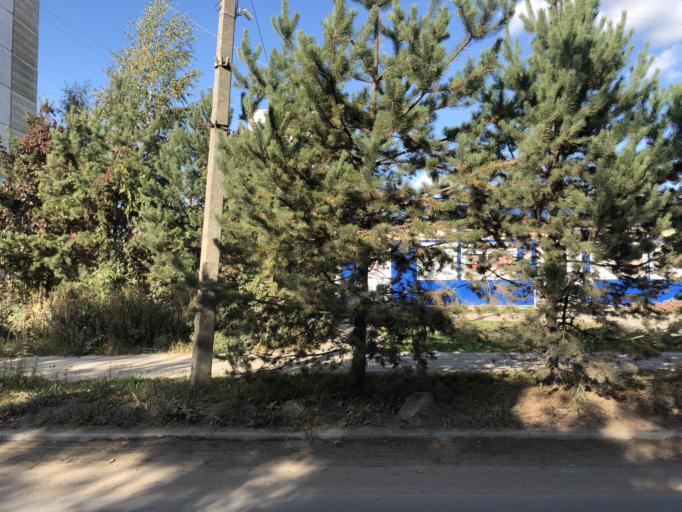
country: RU
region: Tverskaya
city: Rzhev
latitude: 56.2616
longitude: 34.3559
